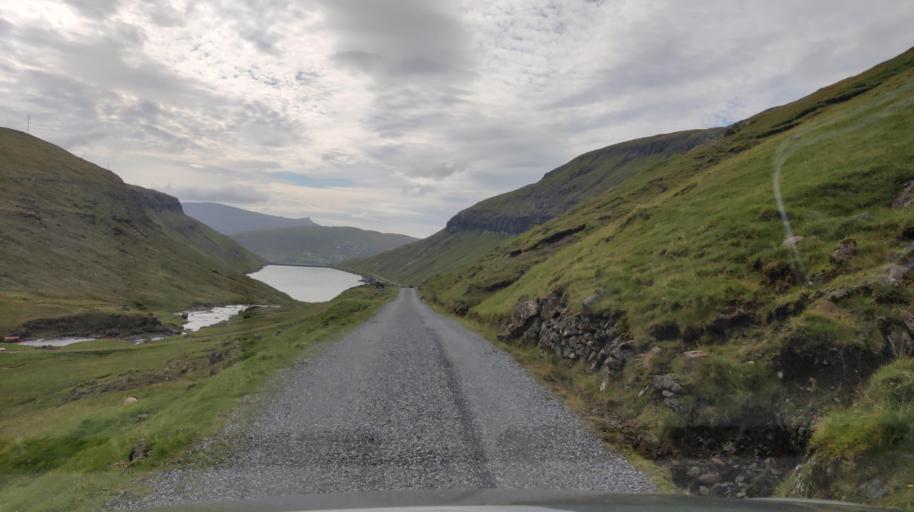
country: FO
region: Streymoy
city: Vestmanna
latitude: 62.1544
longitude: -7.0961
